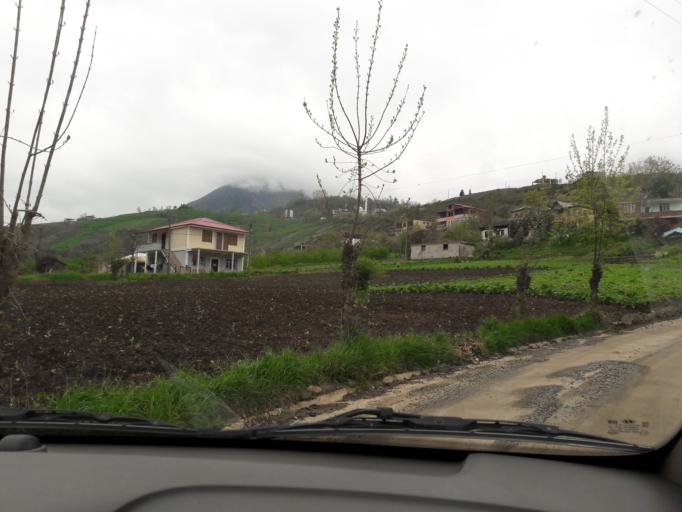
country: TR
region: Trabzon
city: Duzkoy
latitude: 40.9145
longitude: 39.4819
